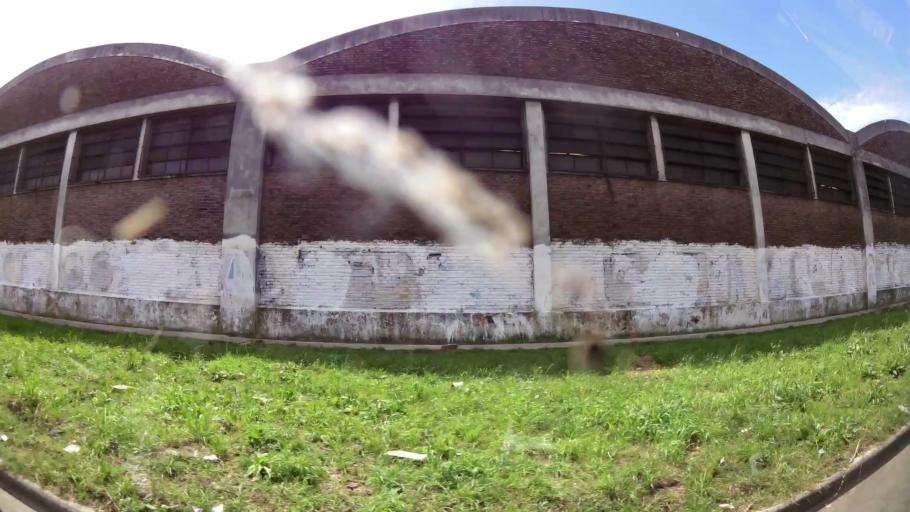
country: AR
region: Buenos Aires
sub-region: Partido de Quilmes
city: Quilmes
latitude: -34.7573
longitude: -58.3005
